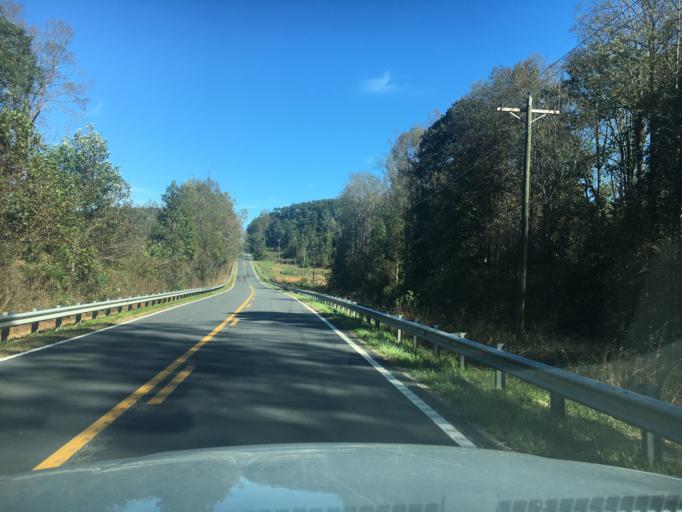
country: US
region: North Carolina
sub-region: Burke County
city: Glen Alpine
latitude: 35.6041
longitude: -81.8176
